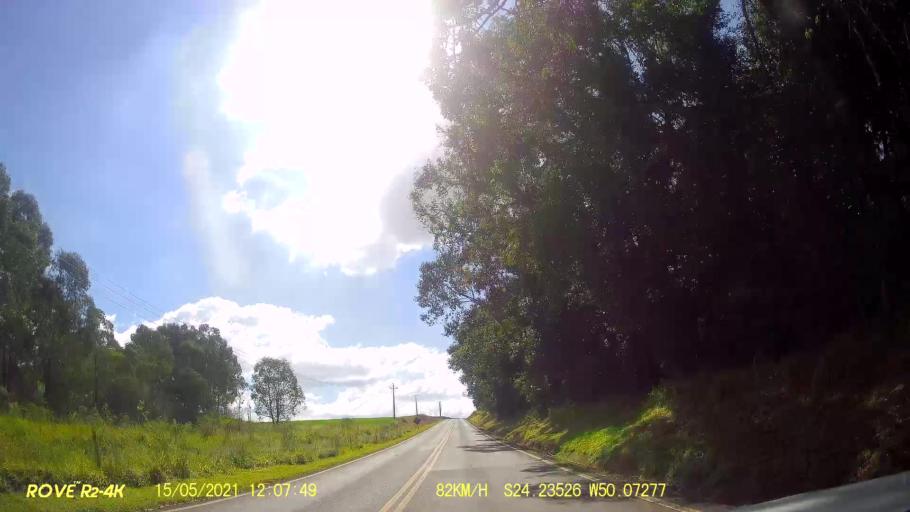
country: BR
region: Parana
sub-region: Pirai Do Sul
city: Pirai do Sul
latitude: -24.2353
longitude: -50.0728
